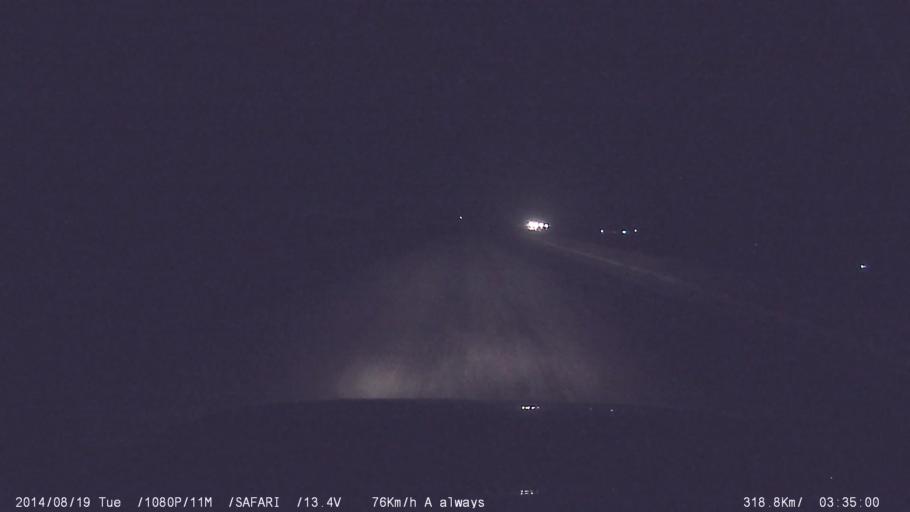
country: IN
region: Tamil Nadu
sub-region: Tiruppur
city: Avinashi
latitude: 11.2153
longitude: 77.3598
